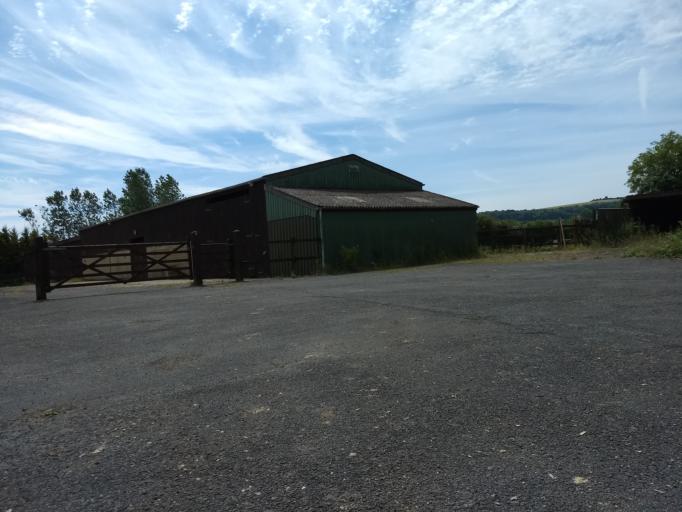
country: GB
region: England
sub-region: Isle of Wight
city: Newport
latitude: 50.7030
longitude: -1.3149
